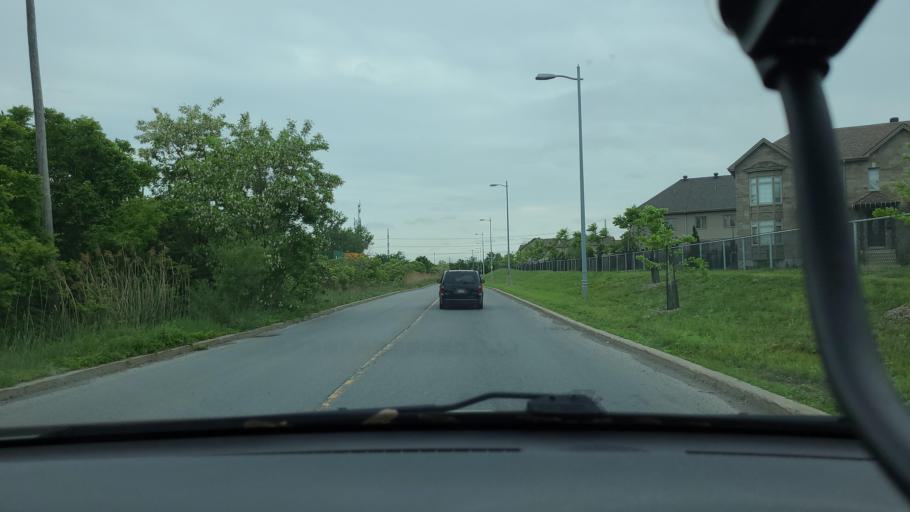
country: CA
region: Quebec
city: Montreal-Ouest
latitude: 45.4474
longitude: -73.6508
